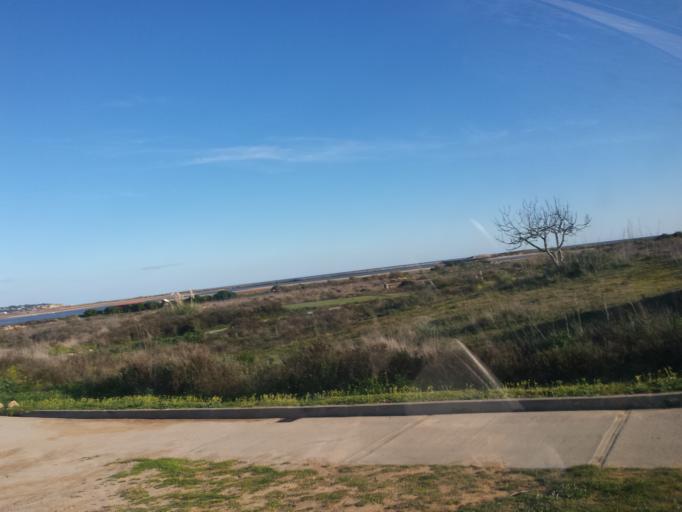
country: PT
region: Faro
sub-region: Portimao
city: Alvor
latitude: 37.1321
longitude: -8.6302
